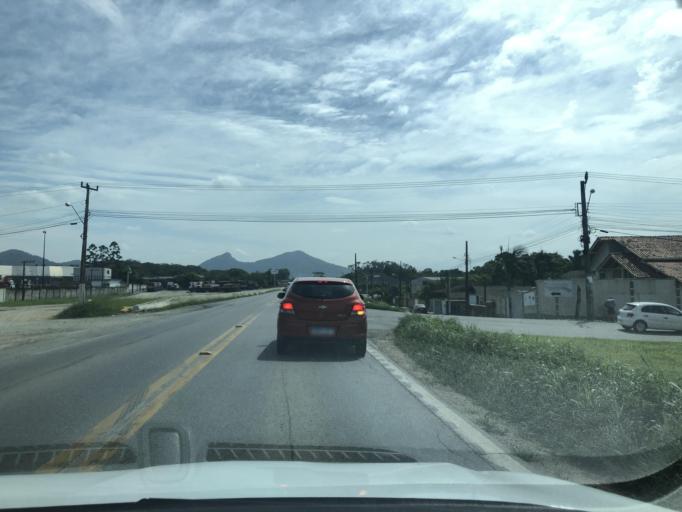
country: BR
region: Santa Catarina
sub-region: Sao Francisco Do Sul
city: Sao Francisco do Sul
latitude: -26.2625
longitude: -48.6290
